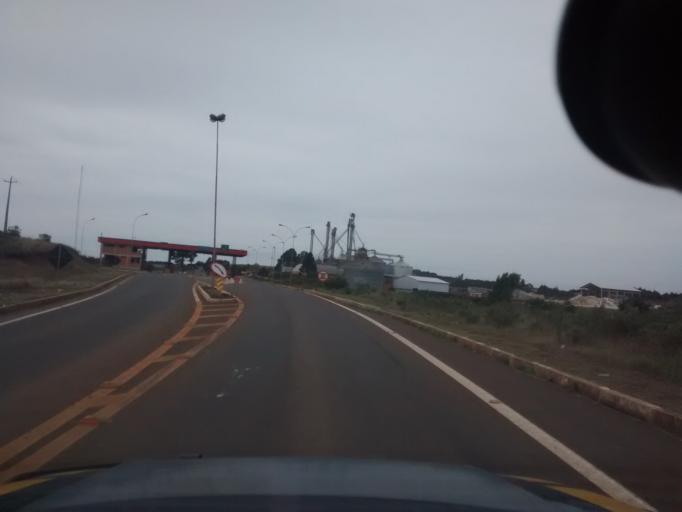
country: BR
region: Rio Grande do Sul
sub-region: Vacaria
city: Vacaria
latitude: -28.4483
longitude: -50.9946
